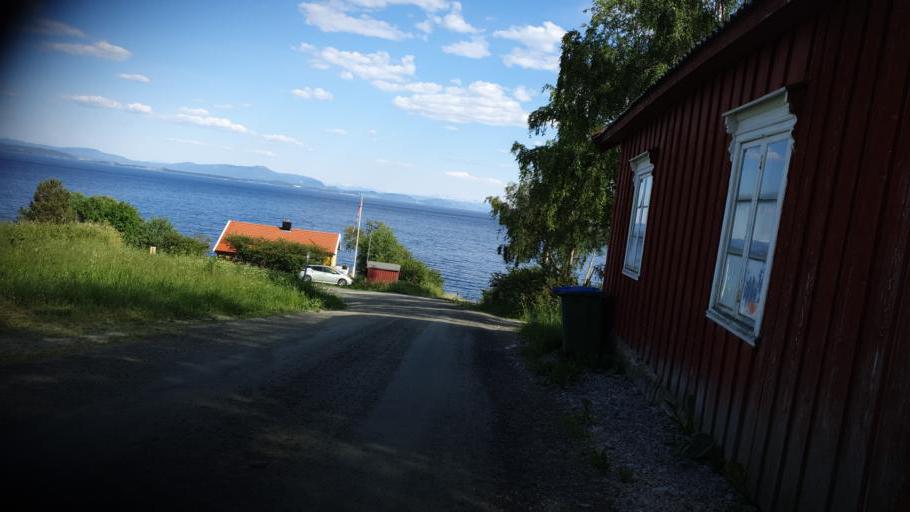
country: NO
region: Sor-Trondelag
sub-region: Trondheim
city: Trondheim
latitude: 63.5823
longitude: 10.4155
